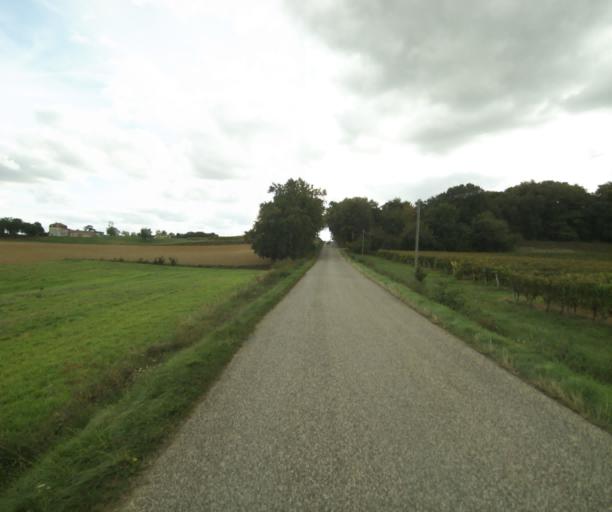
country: FR
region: Midi-Pyrenees
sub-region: Departement du Gers
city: Gondrin
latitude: 43.8708
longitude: 0.2395
